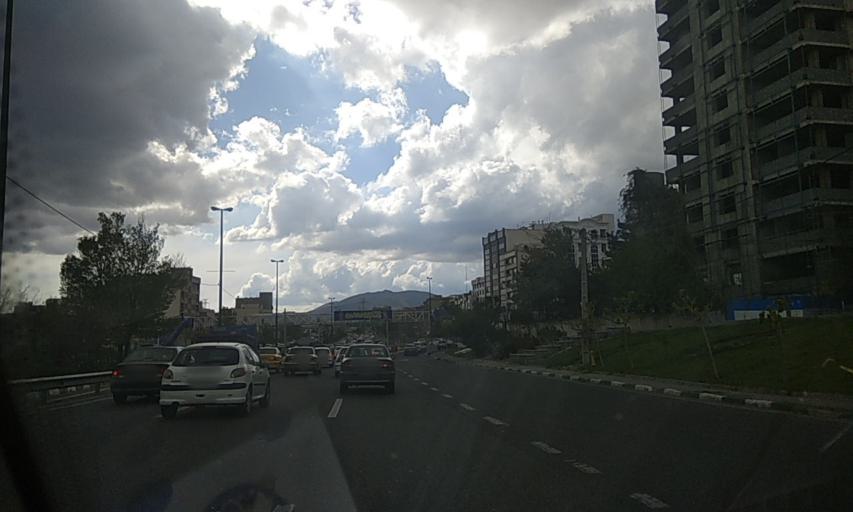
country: IR
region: Tehran
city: Tajrish
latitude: 35.7696
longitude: 51.3291
